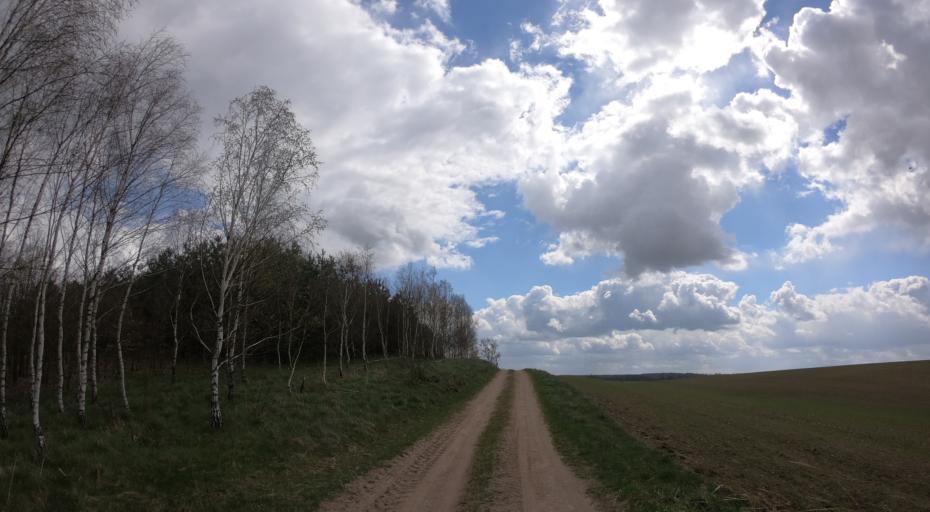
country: PL
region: West Pomeranian Voivodeship
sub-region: Powiat drawski
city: Drawsko Pomorskie
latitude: 53.5530
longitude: 15.8578
